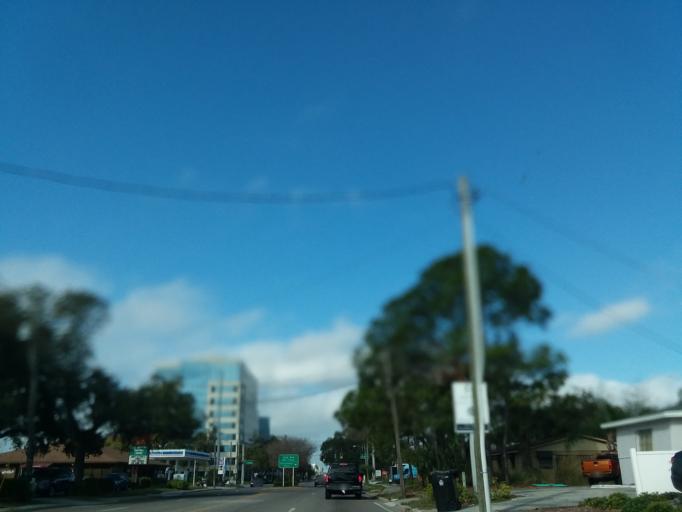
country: US
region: Florida
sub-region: Hillsborough County
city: Tampa
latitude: 27.9522
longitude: -82.5124
